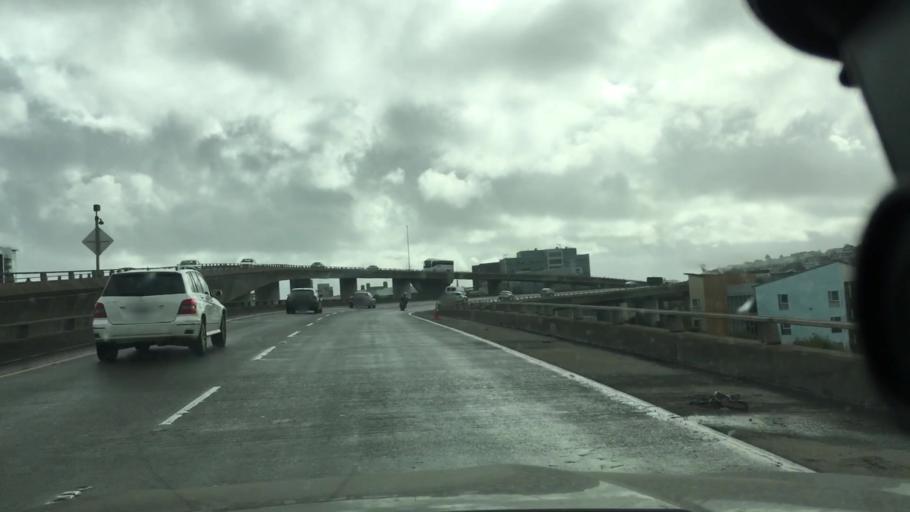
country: US
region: California
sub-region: San Francisco County
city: San Francisco
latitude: 37.7718
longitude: -122.3991
